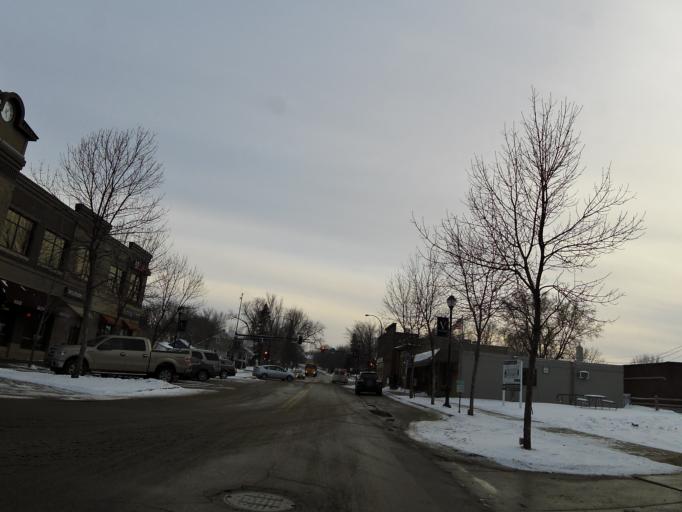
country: US
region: Minnesota
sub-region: Carver County
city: Victoria
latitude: 44.8597
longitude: -93.6620
